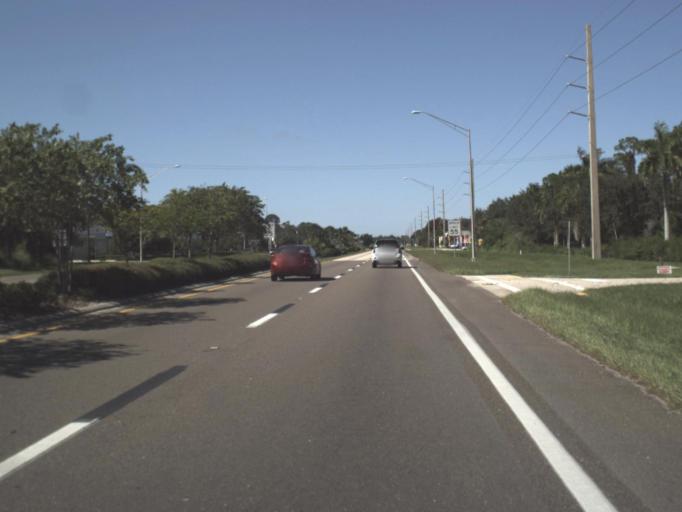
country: US
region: Florida
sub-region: Lee County
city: North Fort Myers
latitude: 26.6691
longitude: -81.8914
